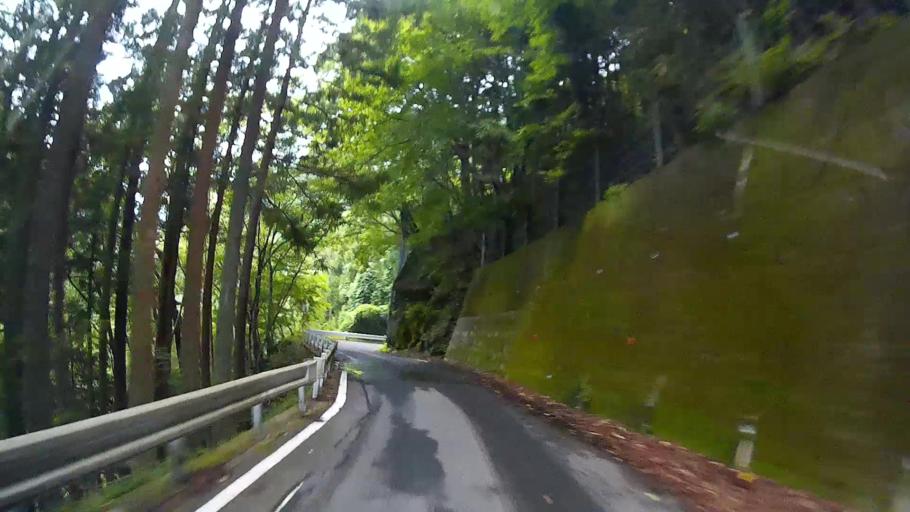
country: JP
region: Saitama
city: Chichibu
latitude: 35.9420
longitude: 138.8589
